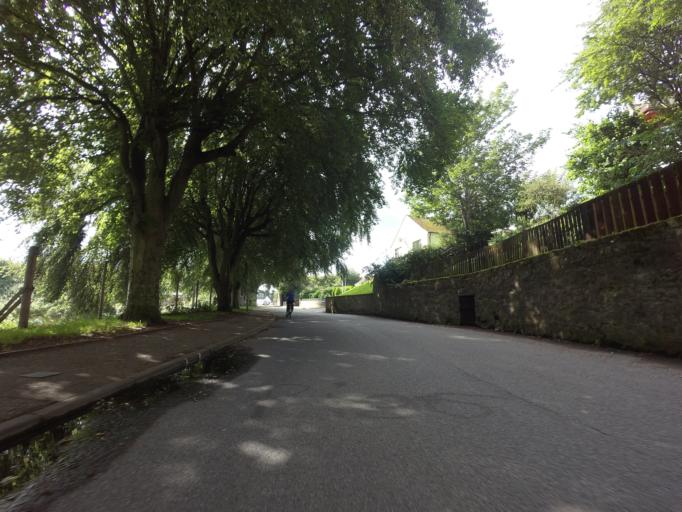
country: GB
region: Scotland
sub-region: Highland
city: Nairn
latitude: 57.5825
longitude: -3.8670
